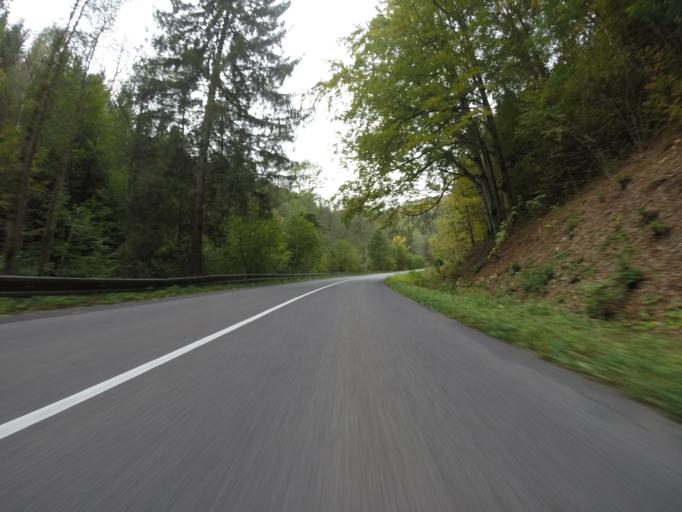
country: SK
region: Banskobystricky
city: Poltar
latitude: 48.5887
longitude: 19.7812
